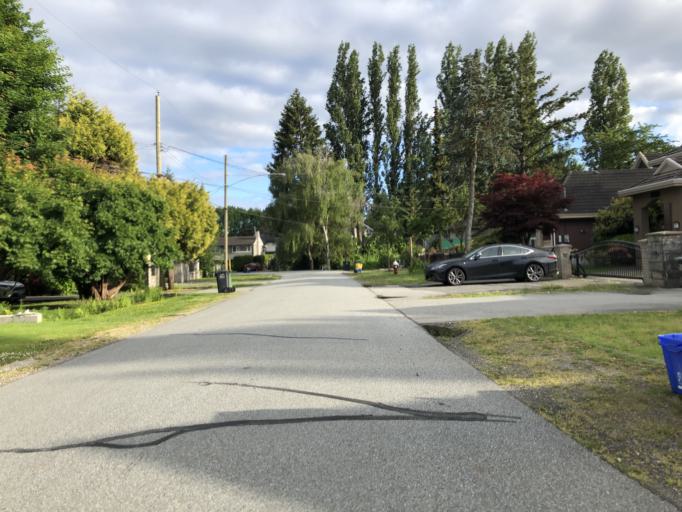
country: CA
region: British Columbia
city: Richmond
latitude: 49.1426
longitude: -123.1240
